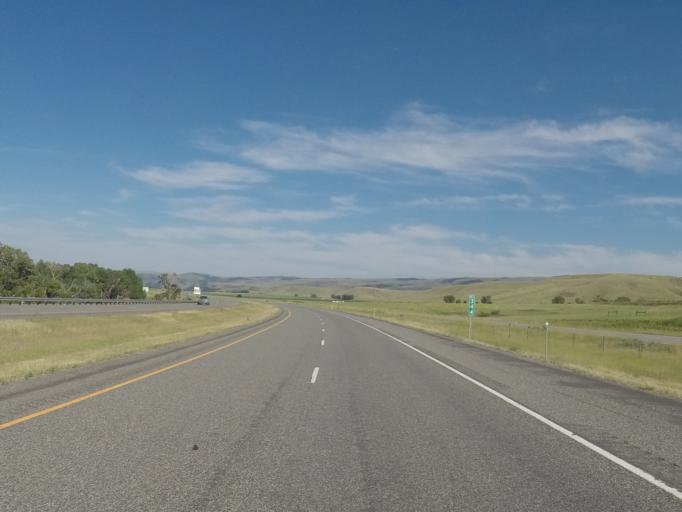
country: US
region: Montana
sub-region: Park County
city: Livingston
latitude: 45.7082
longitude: -110.3857
